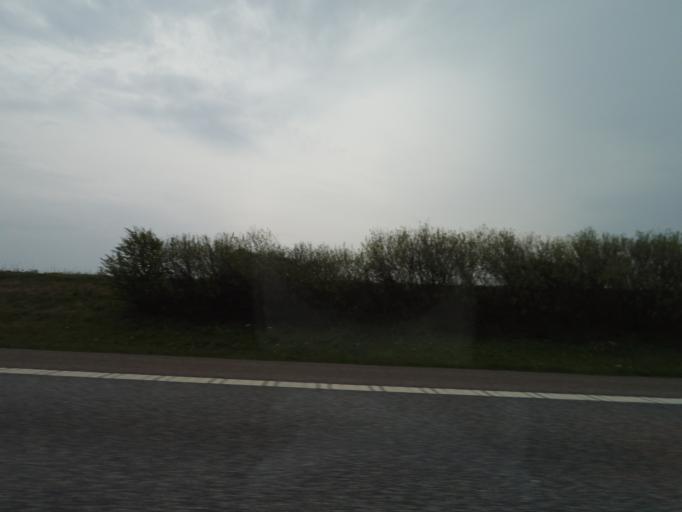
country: DK
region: Central Jutland
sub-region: Hedensted Kommune
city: Hedensted
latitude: 55.7701
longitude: 9.6398
